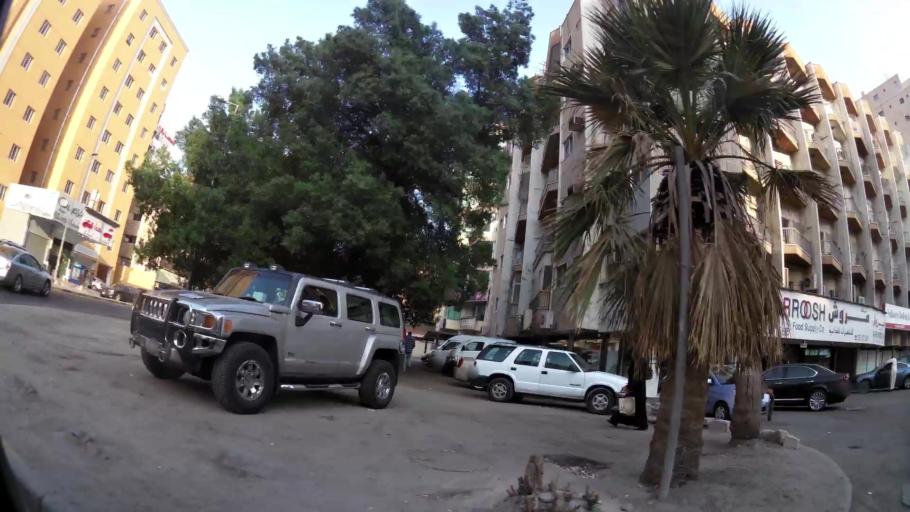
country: KW
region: Muhafazat Hawalli
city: As Salimiyah
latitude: 29.3346
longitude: 48.0540
